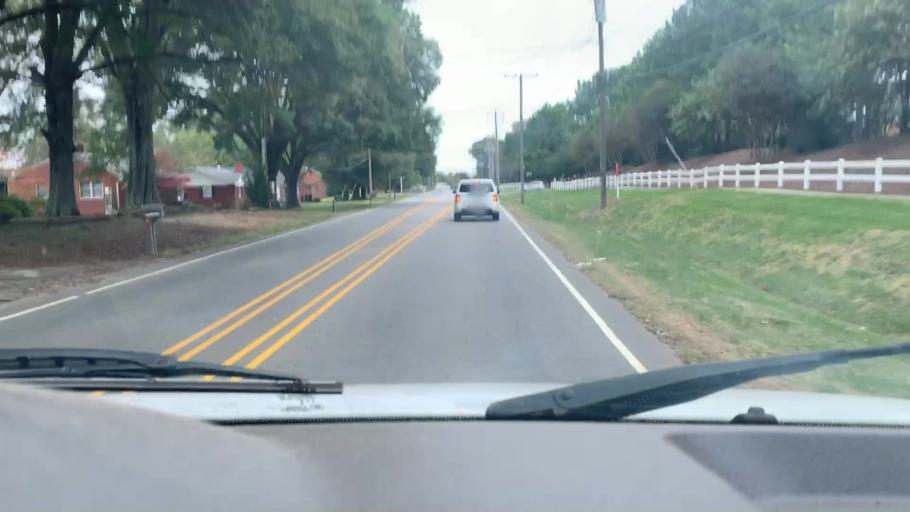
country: US
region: North Carolina
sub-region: Iredell County
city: Mooresville
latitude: 35.5530
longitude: -80.8427
